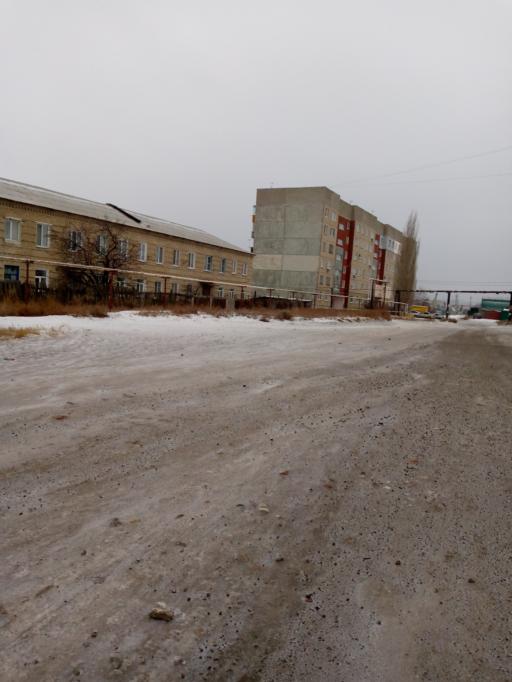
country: RU
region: Saratov
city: Sokolovyy
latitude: 51.3632
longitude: 45.8333
